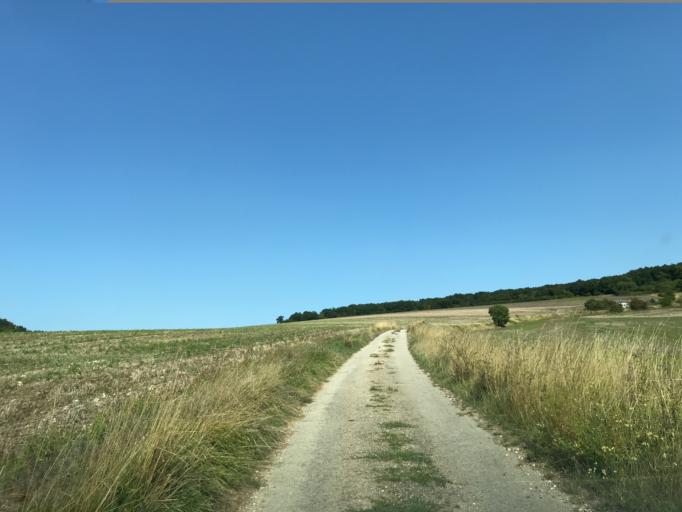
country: FR
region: Haute-Normandie
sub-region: Departement de l'Eure
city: Heudreville-sur-Eure
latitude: 49.1265
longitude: 1.2271
